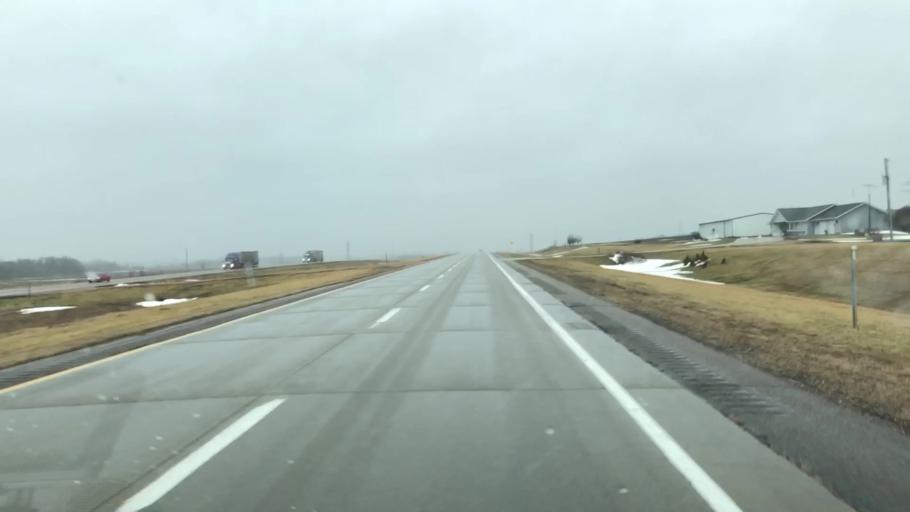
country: US
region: Iowa
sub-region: Sioux County
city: Orange City
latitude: 42.9005
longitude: -96.0864
